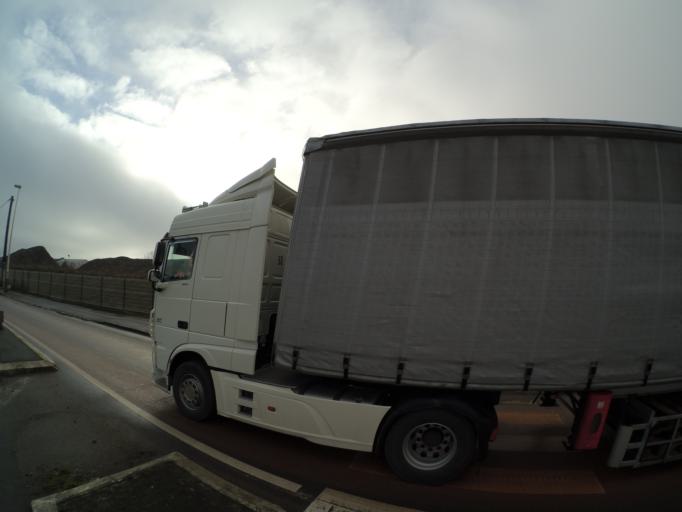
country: FR
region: Pays de la Loire
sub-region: Departement de la Loire-Atlantique
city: Bouguenais
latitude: 47.1943
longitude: -1.6379
